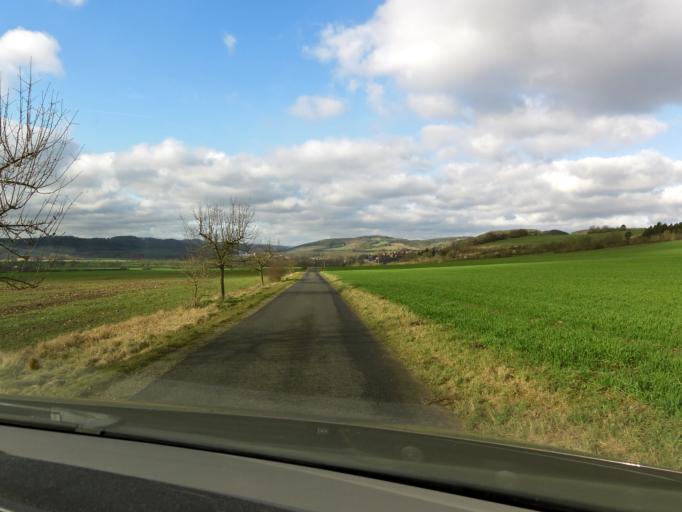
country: DE
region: Thuringia
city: Creuzburg
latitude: 51.0415
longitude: 10.2667
